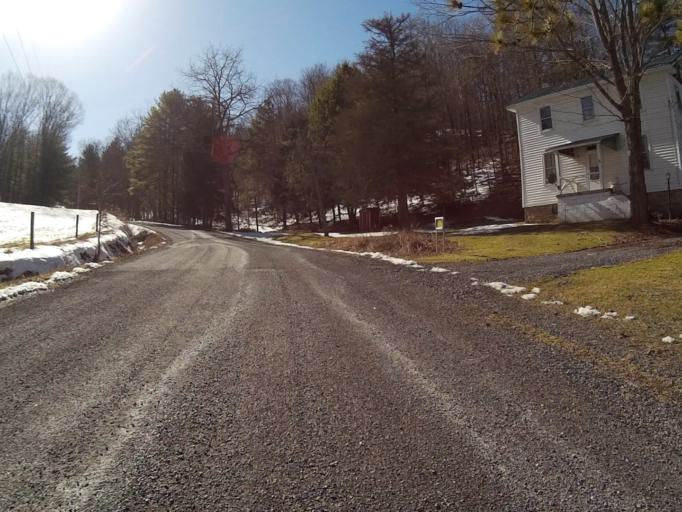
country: US
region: Pennsylvania
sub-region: Centre County
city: Stormstown
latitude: 40.8478
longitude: -78.0350
